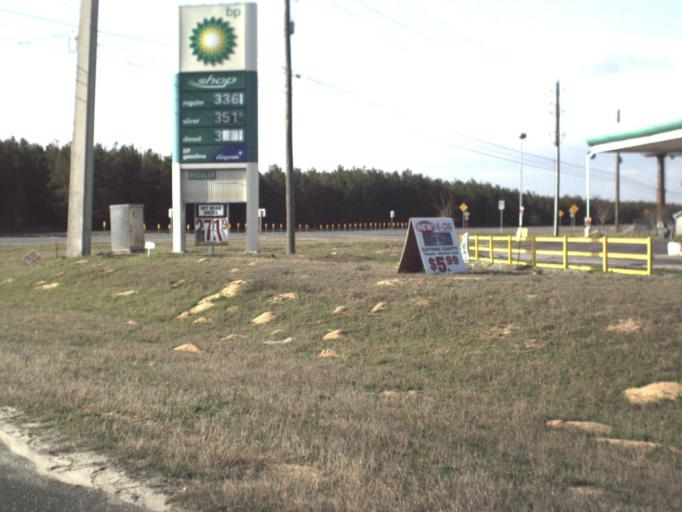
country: US
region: Florida
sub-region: Bay County
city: Lynn Haven
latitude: 30.4312
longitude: -85.6873
